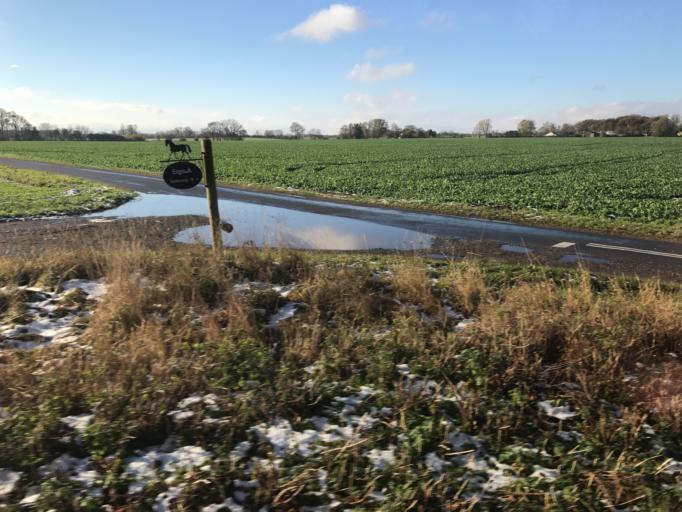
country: DK
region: Zealand
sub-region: Stevns Kommune
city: Store Heddinge
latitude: 55.3411
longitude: 12.3352
